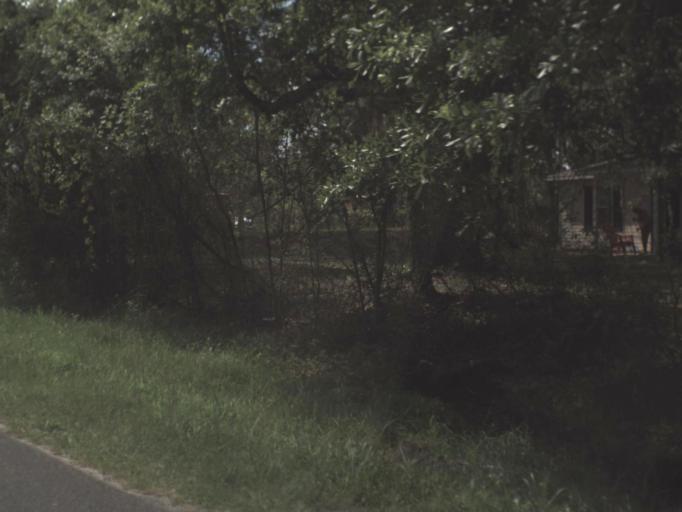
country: US
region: Florida
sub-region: Clay County
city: Green Cove Springs
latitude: 29.9937
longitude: -81.5901
